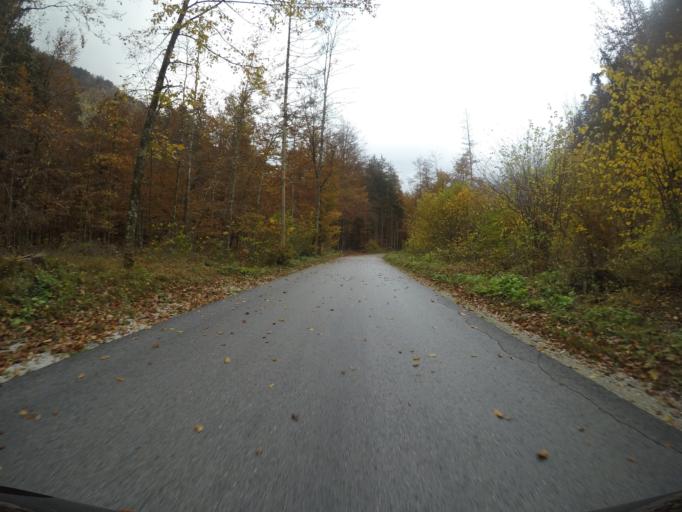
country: SI
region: Jesenice
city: Hrusica
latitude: 46.4271
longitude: 13.9705
